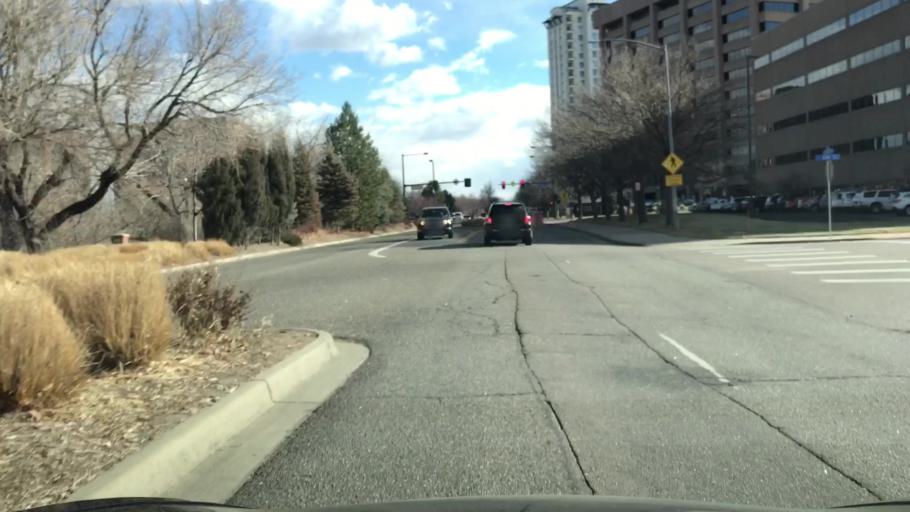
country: US
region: Colorado
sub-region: Arapahoe County
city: Glendale
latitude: 39.7055
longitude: -104.9378
